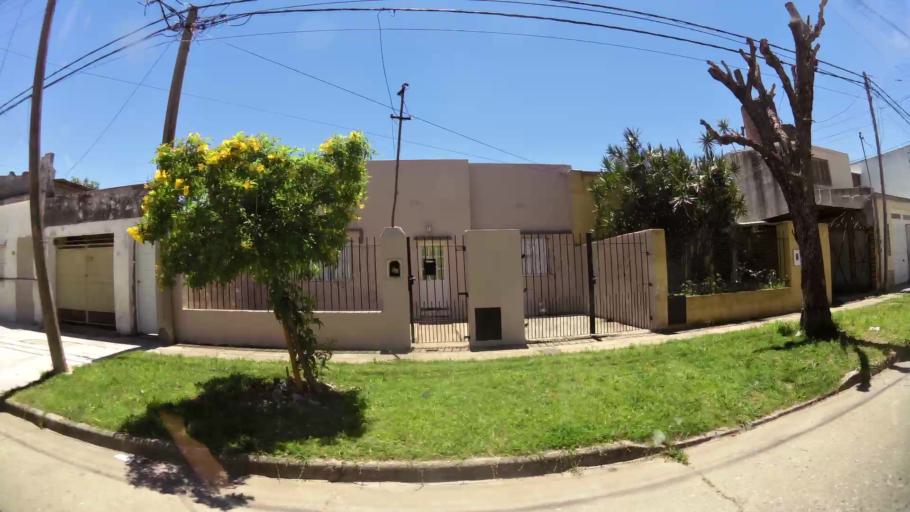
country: AR
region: Santa Fe
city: Santa Fe de la Vera Cruz
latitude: -31.6480
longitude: -60.7256
